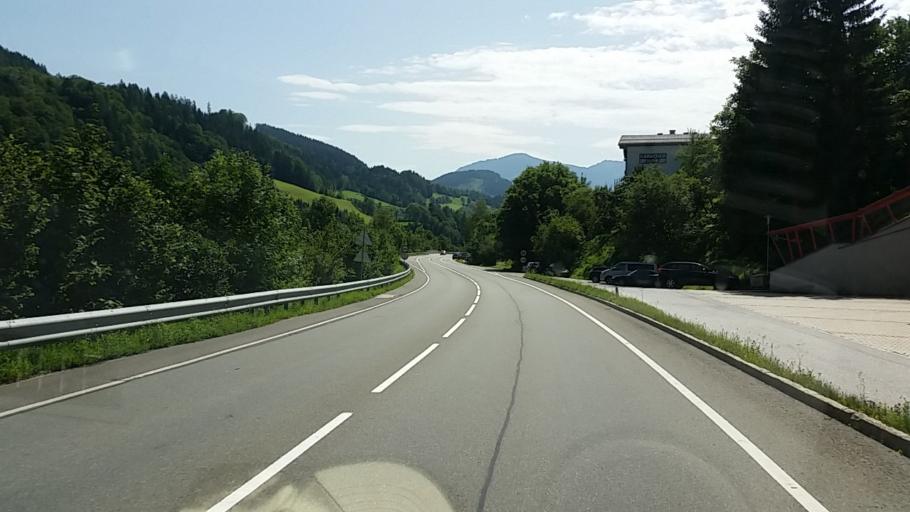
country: AT
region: Salzburg
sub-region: Politischer Bezirk Sankt Johann im Pongau
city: Werfen
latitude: 47.4775
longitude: 13.1893
